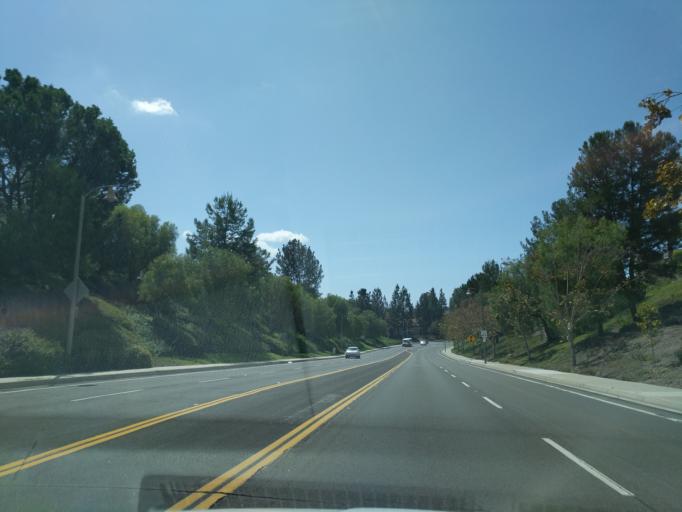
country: US
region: California
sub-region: Orange County
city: Ladera Ranch
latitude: 33.5769
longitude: -117.6523
